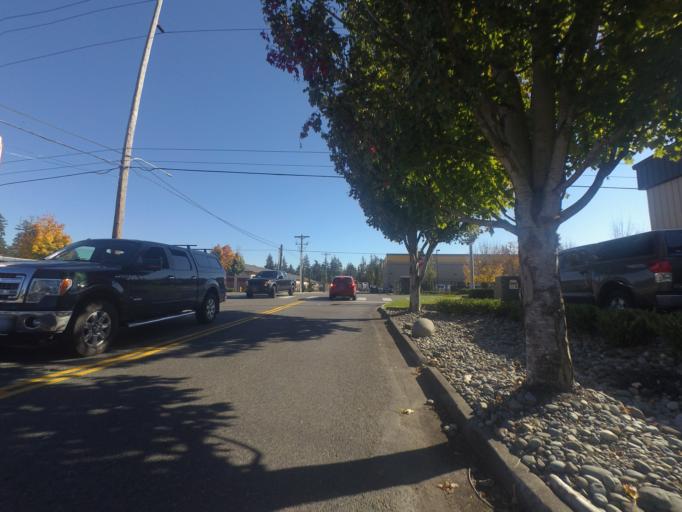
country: US
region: Washington
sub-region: Pierce County
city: McChord Air Force Base
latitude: 47.1449
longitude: -122.5125
